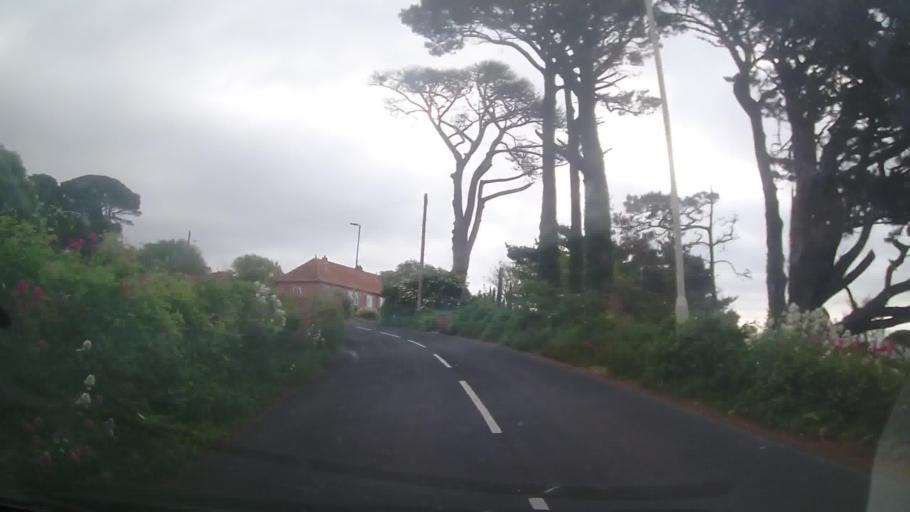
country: GB
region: England
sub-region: Devon
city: Dartmouth
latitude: 50.3209
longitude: -3.5990
